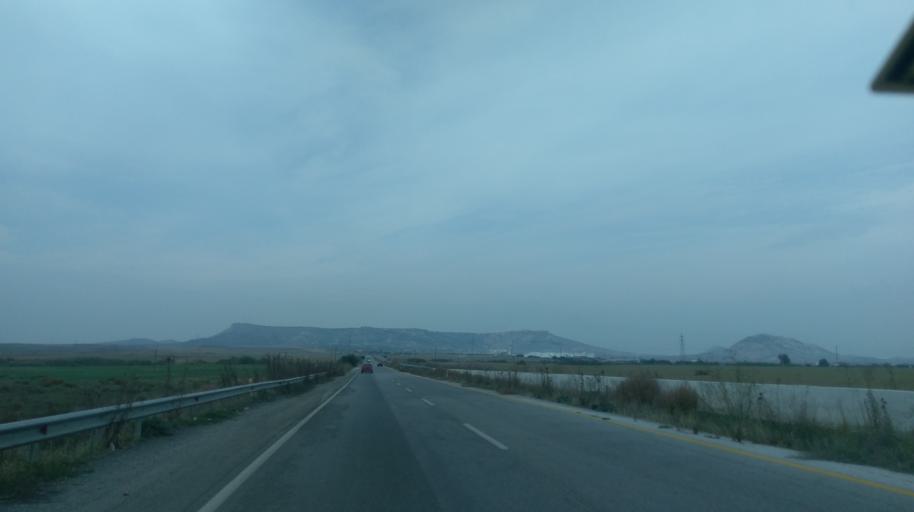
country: CY
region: Lefkosia
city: Mammari
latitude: 35.2194
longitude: 33.1718
